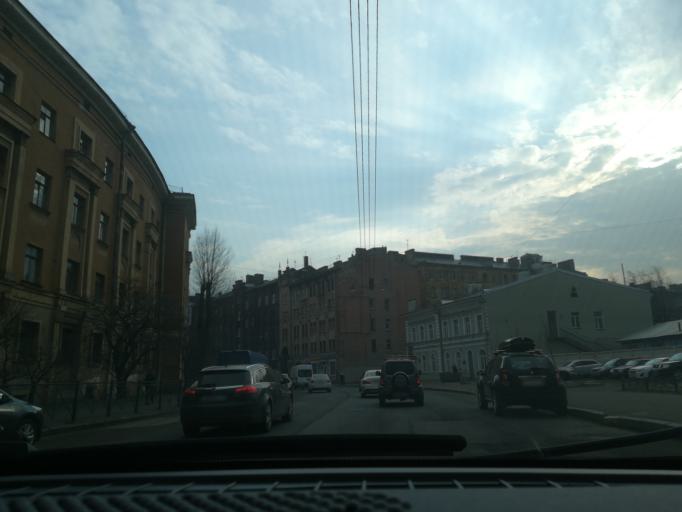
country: RU
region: St.-Petersburg
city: Admiralteisky
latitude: 59.9057
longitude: 30.2752
